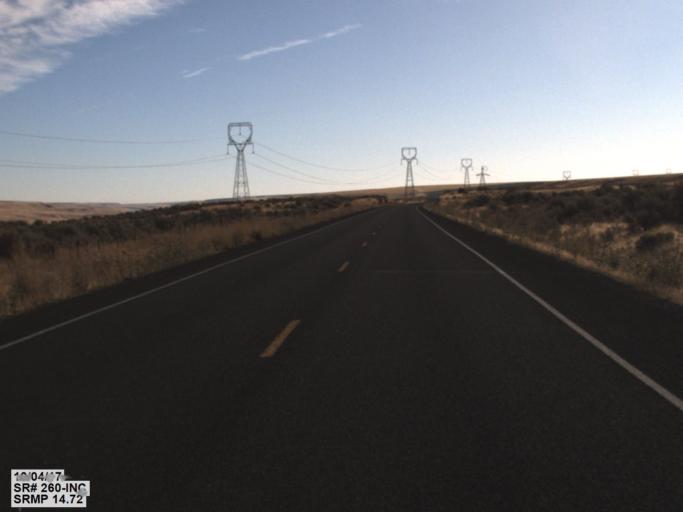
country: US
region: Washington
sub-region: Franklin County
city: Connell
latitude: 46.6309
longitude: -118.7426
